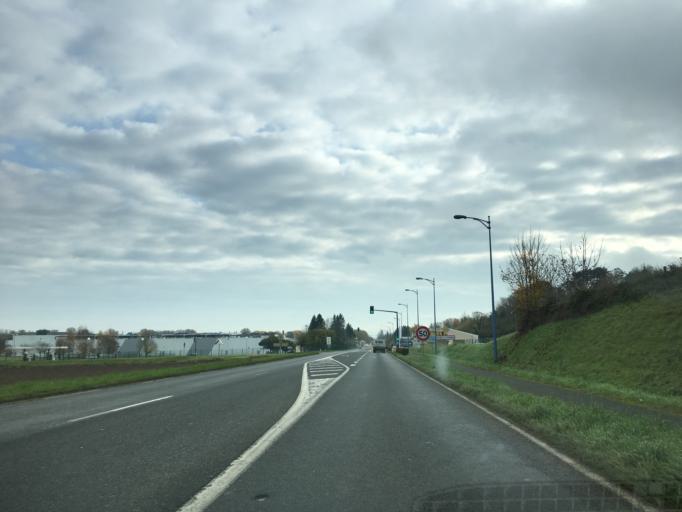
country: FR
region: Bourgogne
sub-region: Departement de l'Yonne
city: Pont-sur-Yonne
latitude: 48.2950
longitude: 3.1933
